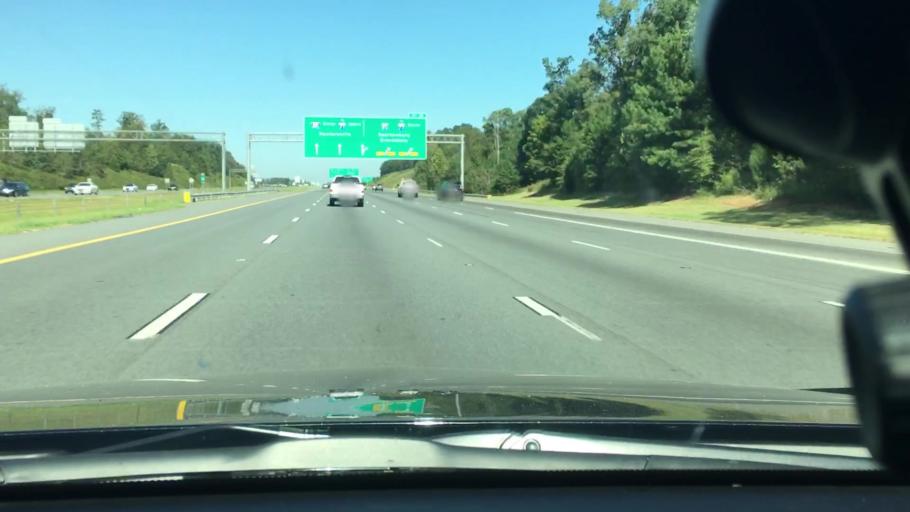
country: US
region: North Carolina
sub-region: Cabarrus County
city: Harrisburg
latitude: 35.3366
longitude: -80.7236
